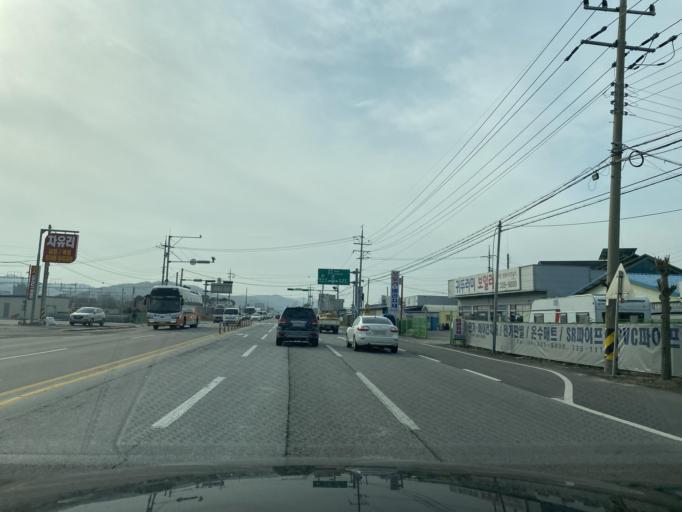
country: KR
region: Chungcheongnam-do
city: Yesan
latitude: 36.6918
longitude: 126.8279
